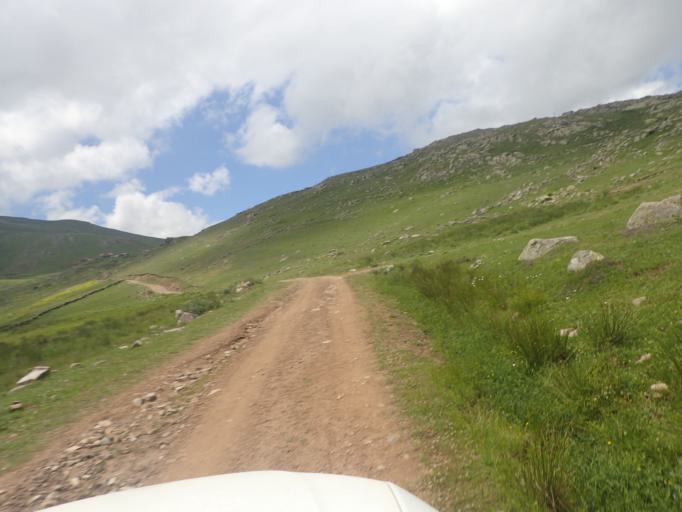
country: TR
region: Ordu
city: Yesilce
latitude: 40.5731
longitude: 37.9621
